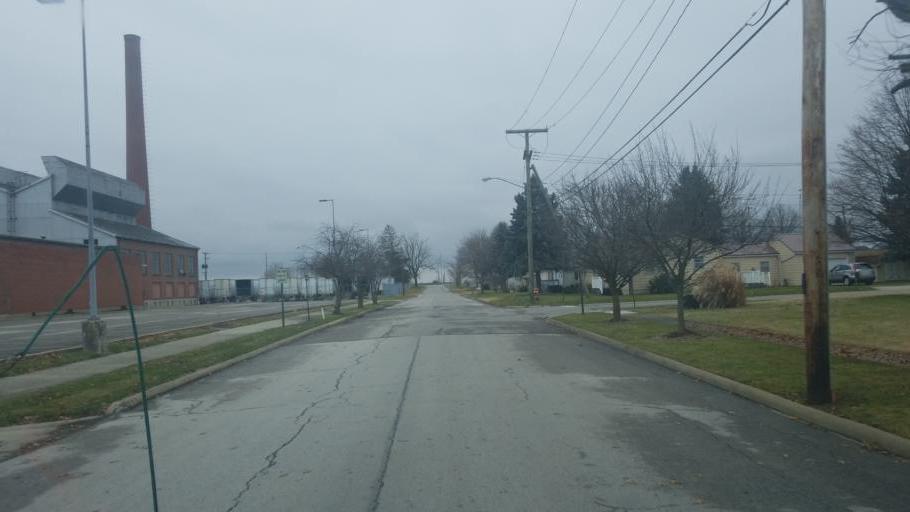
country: US
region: Ohio
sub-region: Crawford County
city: Bucyrus
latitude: 40.7936
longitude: -82.9740
